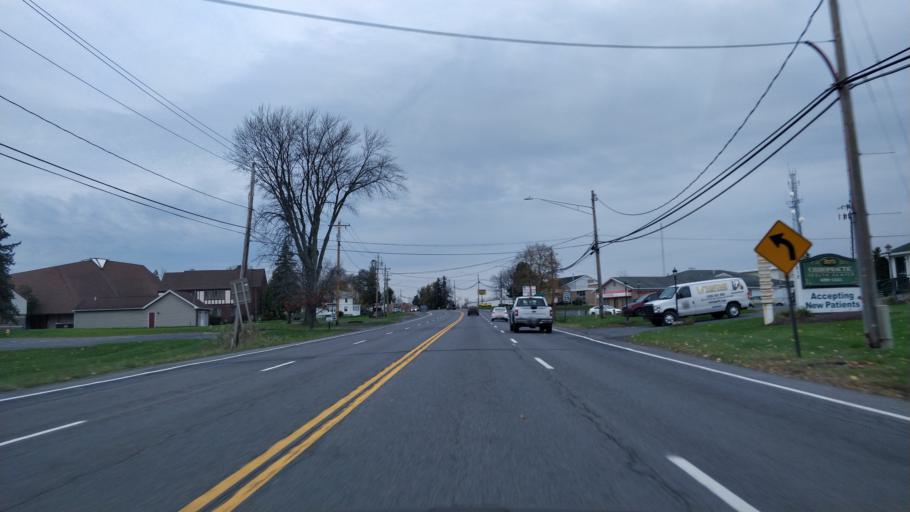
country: US
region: New York
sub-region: Onondaga County
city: North Syracuse
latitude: 43.1675
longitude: -76.1179
